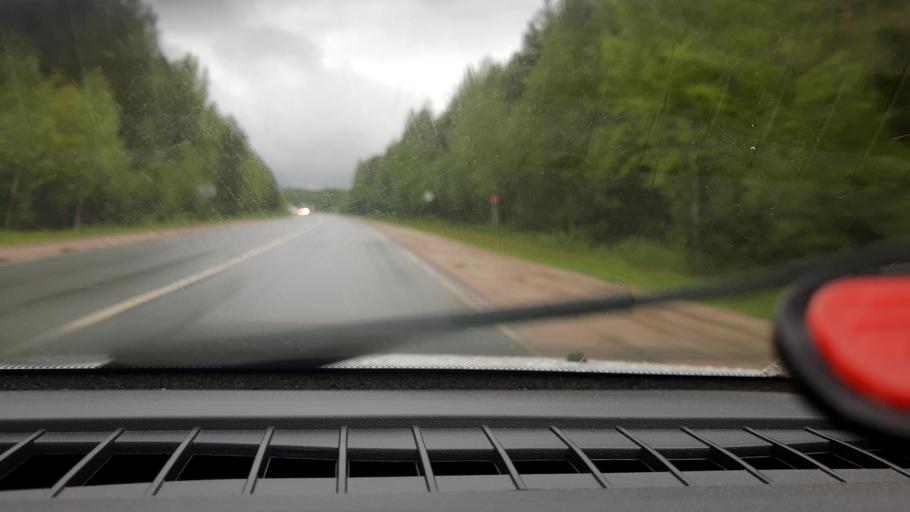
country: RU
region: Nizjnij Novgorod
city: Semenov
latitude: 56.7670
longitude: 44.4090
